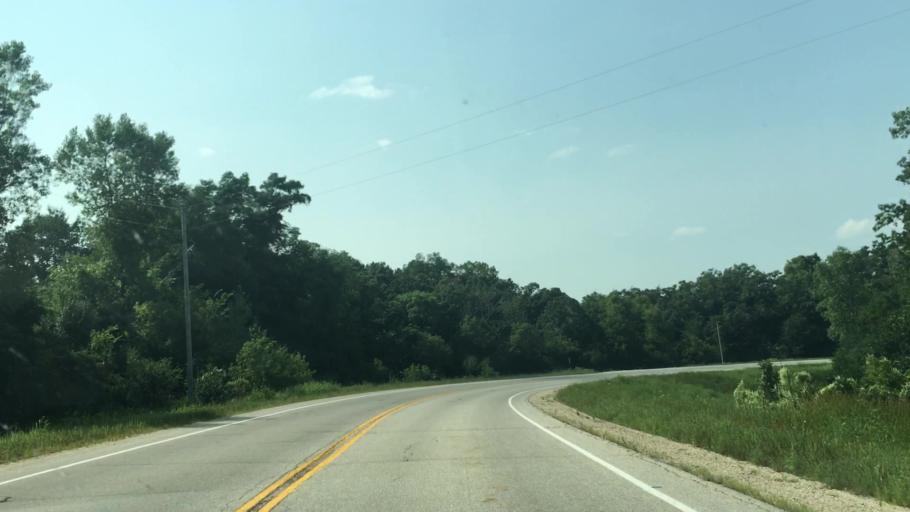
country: US
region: Minnesota
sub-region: Fillmore County
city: Preston
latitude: 43.7013
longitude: -91.9690
